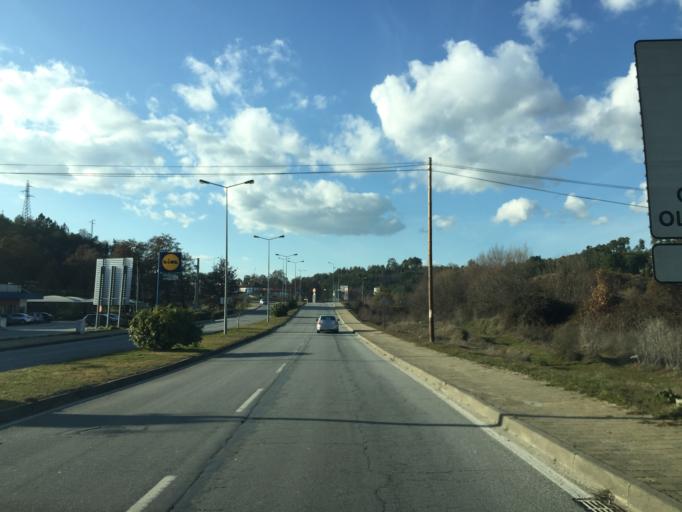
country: PT
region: Guarda
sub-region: Seia
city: Seia
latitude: 40.4301
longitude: -7.7161
